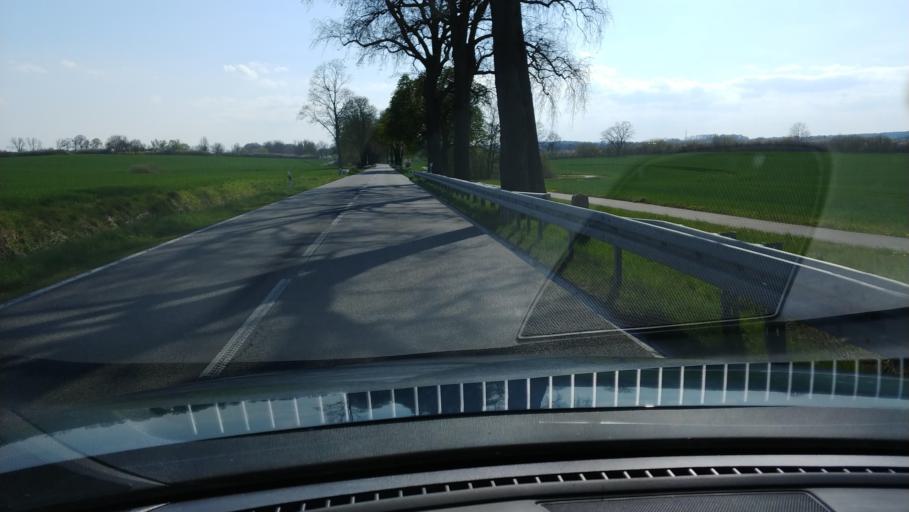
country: DE
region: Mecklenburg-Vorpommern
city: Muhlen Eichsen
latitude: 53.7716
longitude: 11.2702
